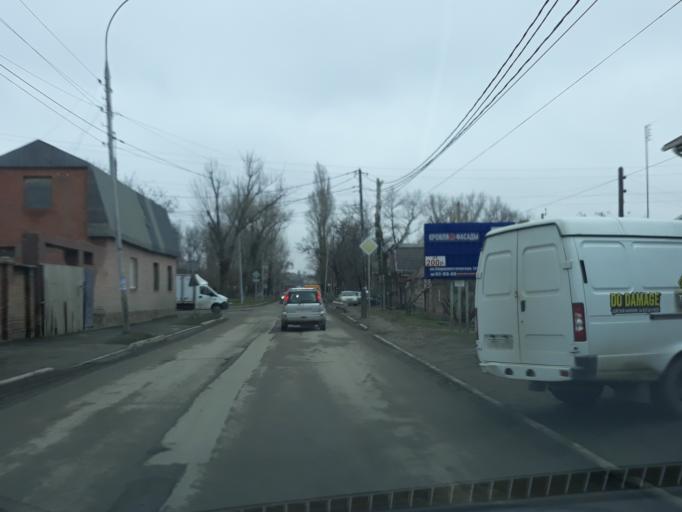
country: RU
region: Rostov
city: Taganrog
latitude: 47.2351
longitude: 38.9264
